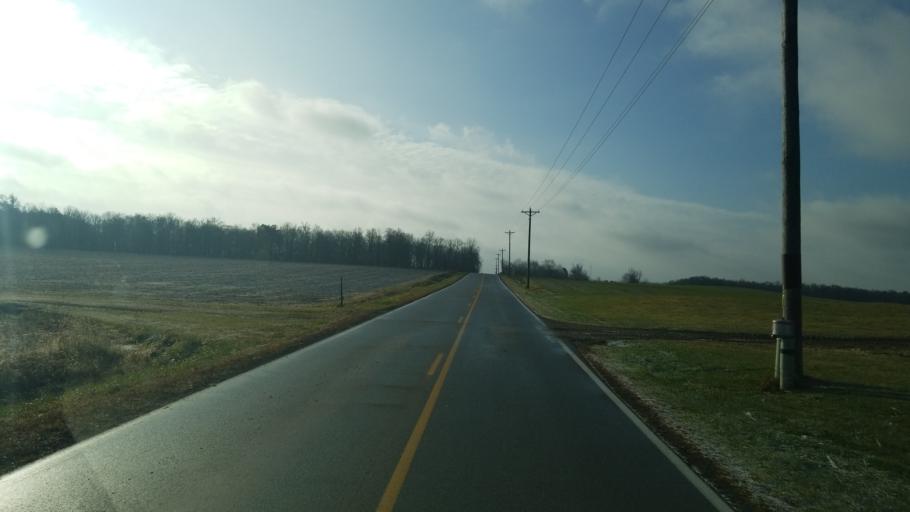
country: US
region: Ohio
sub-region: Richland County
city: Shelby
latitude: 40.9204
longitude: -82.7434
